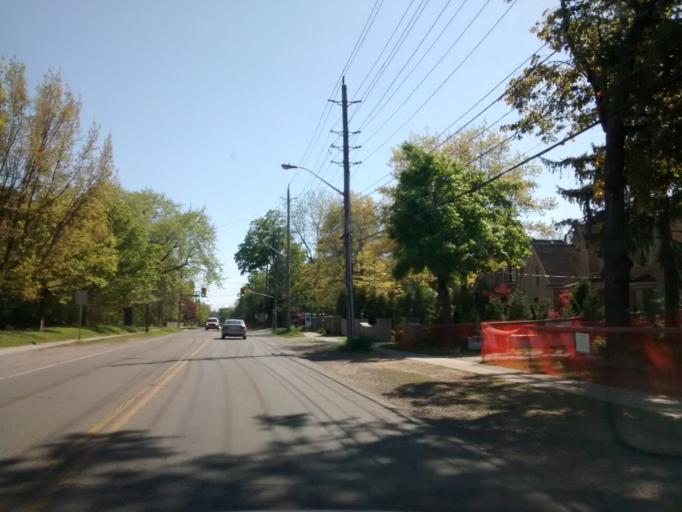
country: CA
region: Ontario
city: Oakville
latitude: 43.4329
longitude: -79.6820
